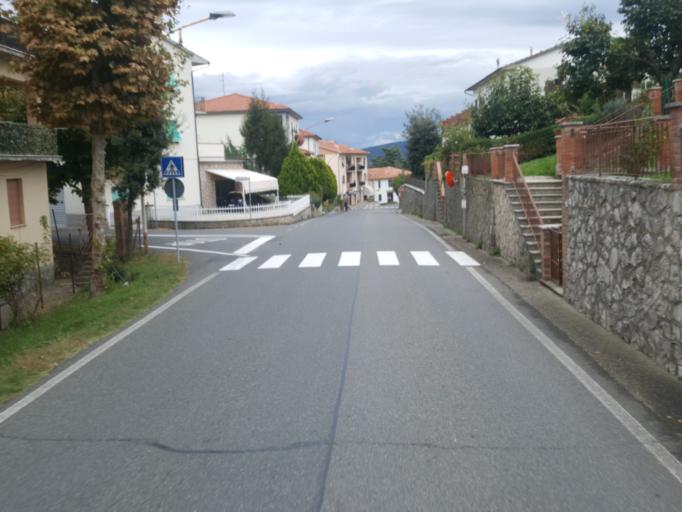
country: IT
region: Tuscany
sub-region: Province of Pisa
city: Castelnuovo di Val di Cecina
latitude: 43.2105
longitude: 10.9010
